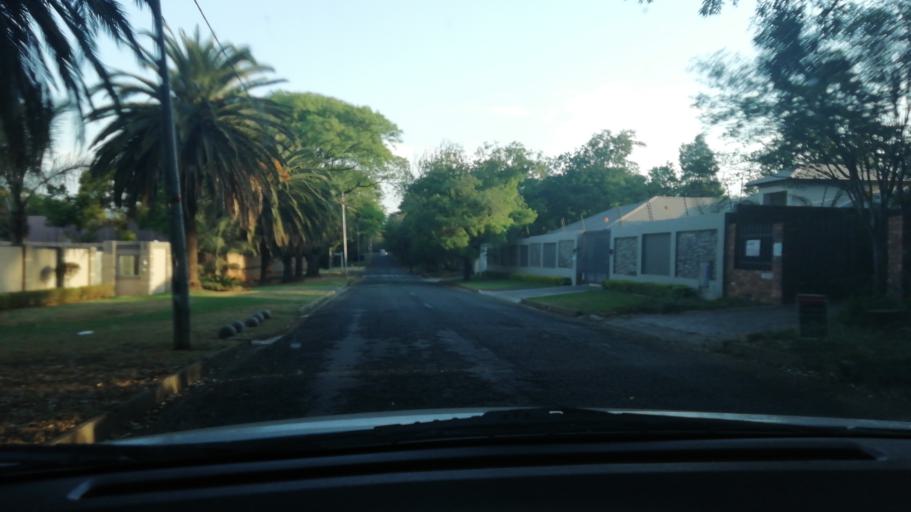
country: ZA
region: Gauteng
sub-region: Ekurhuleni Metropolitan Municipality
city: Benoni
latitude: -26.1927
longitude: 28.2885
